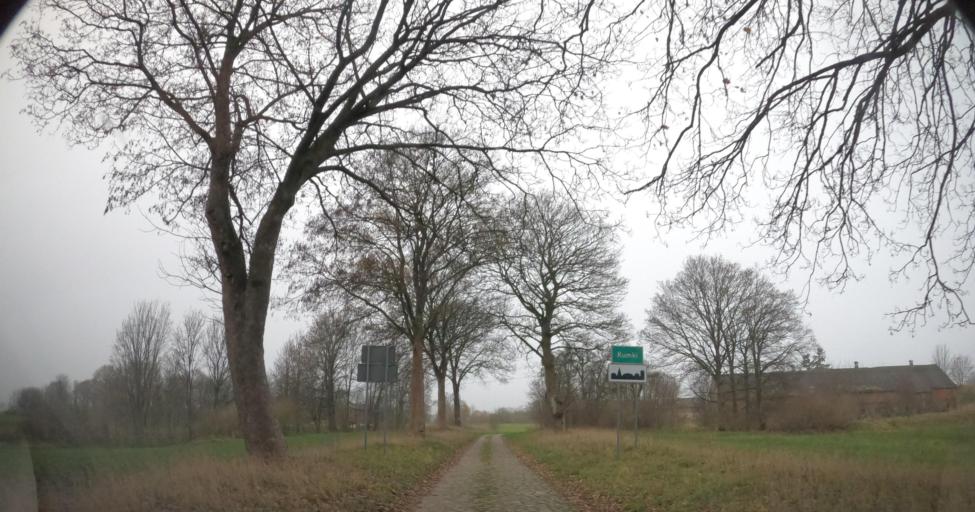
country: PL
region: West Pomeranian Voivodeship
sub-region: Powiat drawski
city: Drawsko Pomorskie
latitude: 53.5422
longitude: 15.7283
